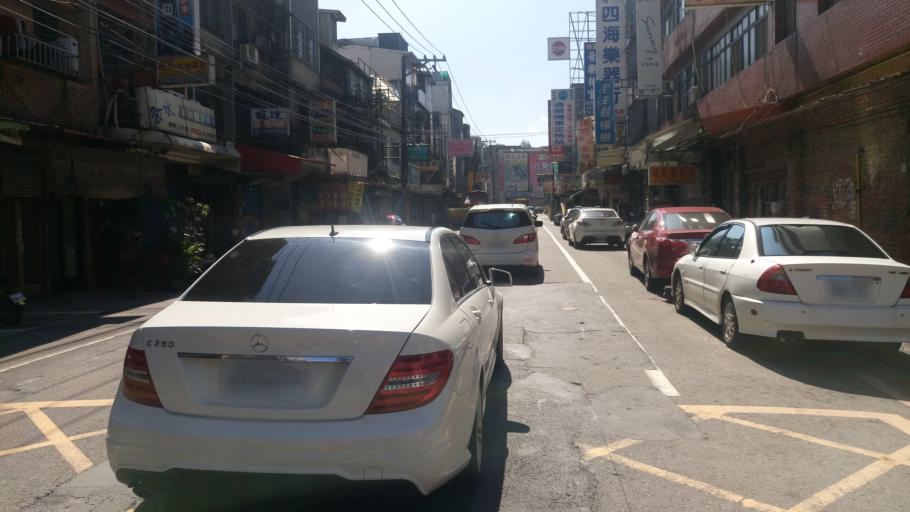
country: TW
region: Taiwan
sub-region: Hsinchu
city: Zhubei
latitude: 24.7348
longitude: 121.0886
